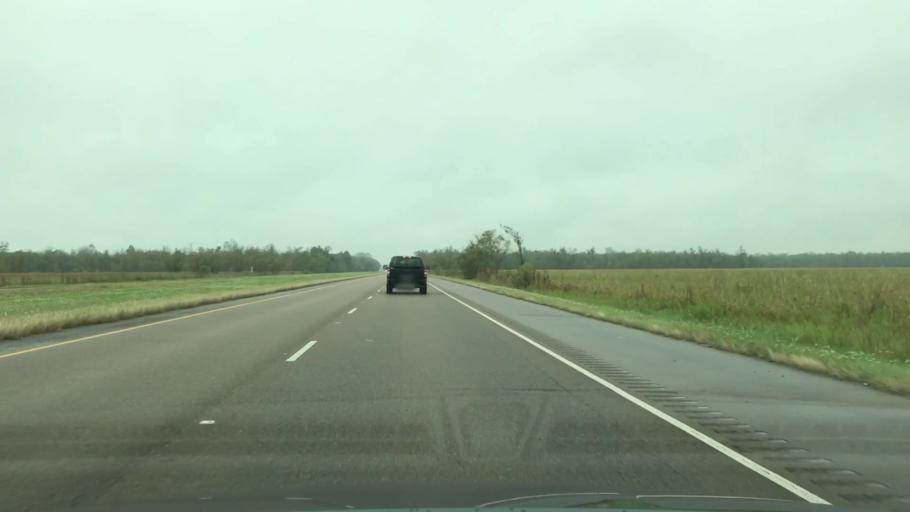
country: US
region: Louisiana
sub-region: Terrebonne Parish
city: Bayou Cane
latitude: 29.6878
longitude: -90.6862
